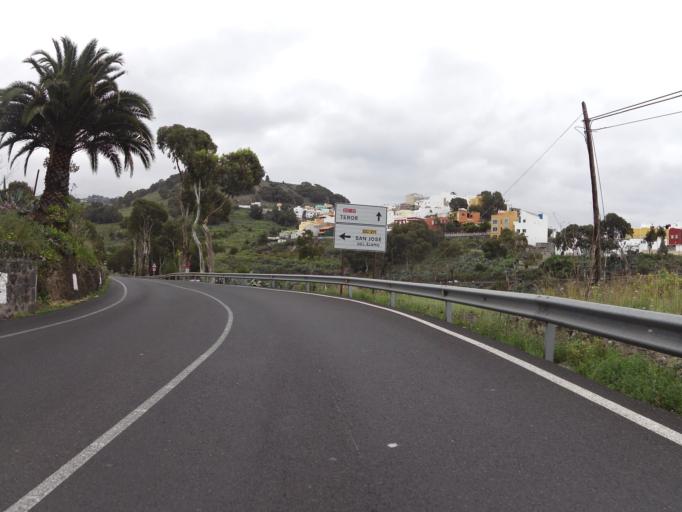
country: ES
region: Canary Islands
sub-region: Provincia de Las Palmas
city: Arucas
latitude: 28.0946
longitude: -15.4947
